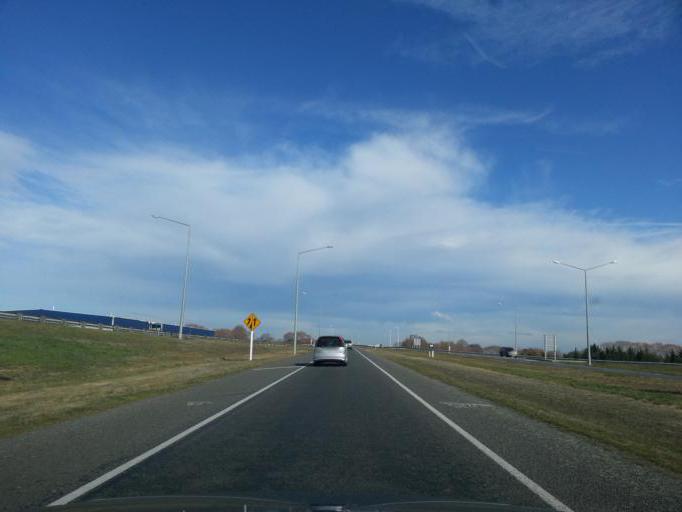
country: NZ
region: Canterbury
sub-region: Waimakariri District
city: Kaiapoi
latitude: -43.3751
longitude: 172.6465
